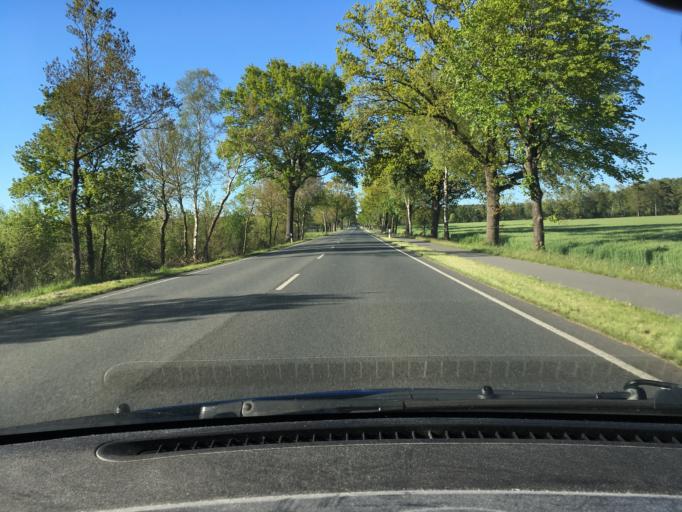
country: DE
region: Lower Saxony
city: Soltau
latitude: 53.0309
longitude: 9.8519
